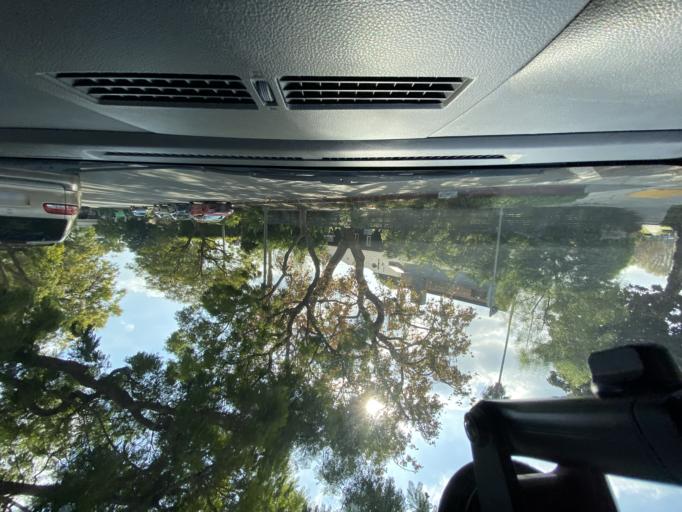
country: US
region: California
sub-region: Los Angeles County
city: Westwood, Los Angeles
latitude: 34.0241
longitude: -118.4336
